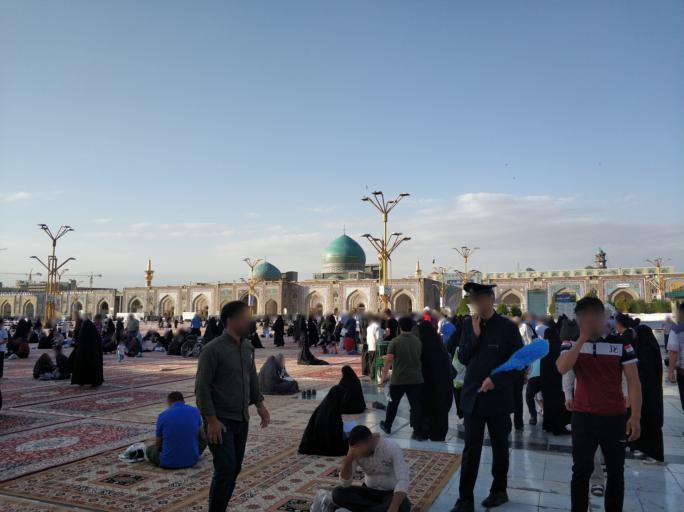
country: IR
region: Razavi Khorasan
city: Mashhad
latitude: 36.2855
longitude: 59.6134
